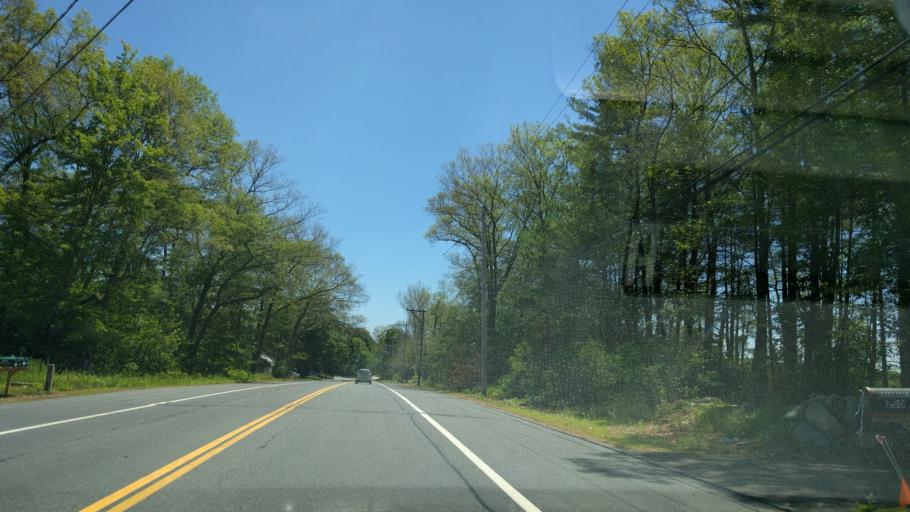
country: US
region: Massachusetts
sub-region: Worcester County
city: Millville
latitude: 42.0121
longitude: -71.5920
